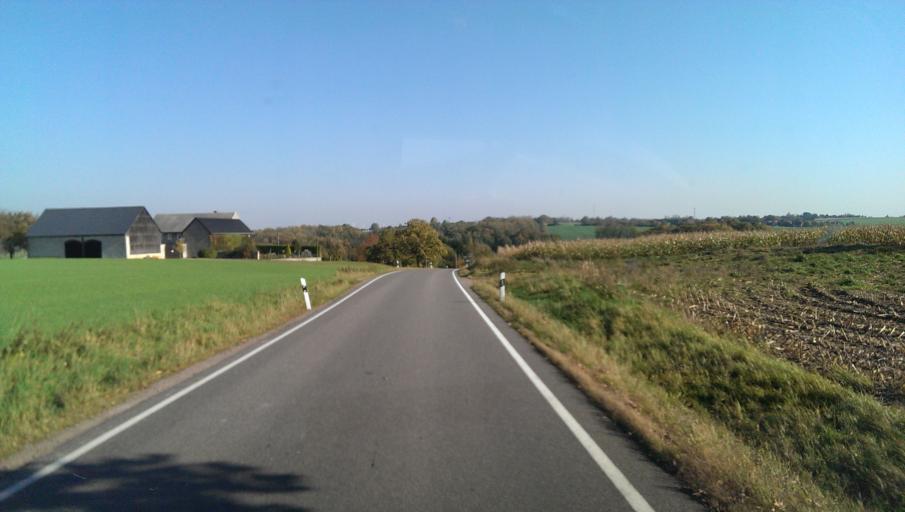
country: DE
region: Saxony
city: Dobeln
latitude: 51.1065
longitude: 13.0694
